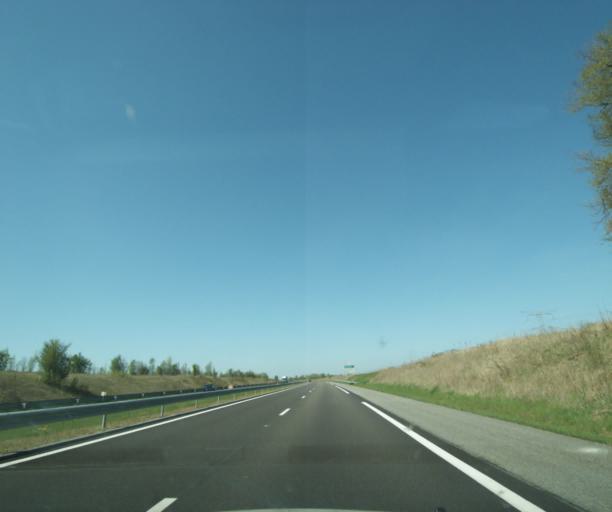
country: FR
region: Bourgogne
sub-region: Departement de la Nievre
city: Neuvy-sur-Loire
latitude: 47.5581
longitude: 2.8834
